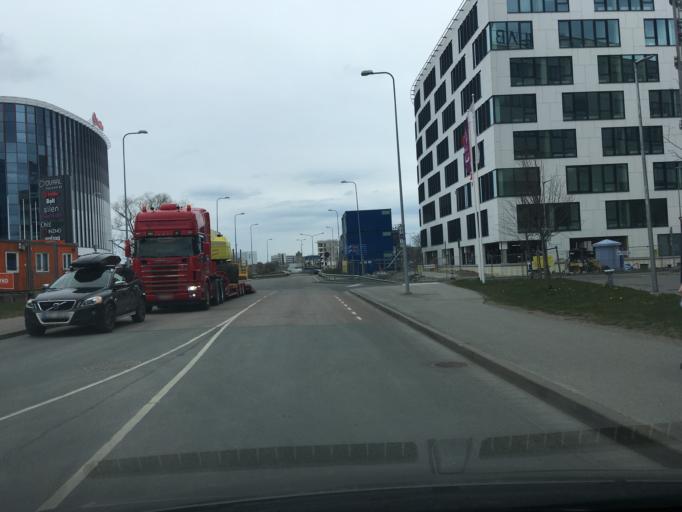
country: EE
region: Harju
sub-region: Tallinna linn
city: Tallinn
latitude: 59.4173
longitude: 24.7529
